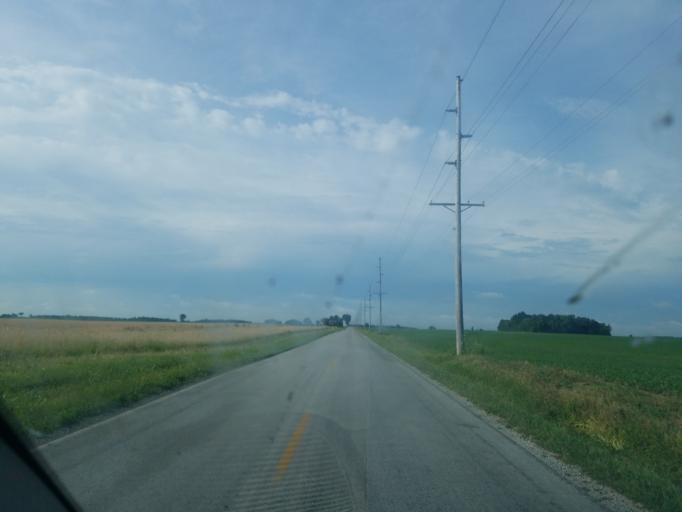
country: US
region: Ohio
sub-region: Hardin County
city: Forest
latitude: 40.8006
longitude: -83.4967
